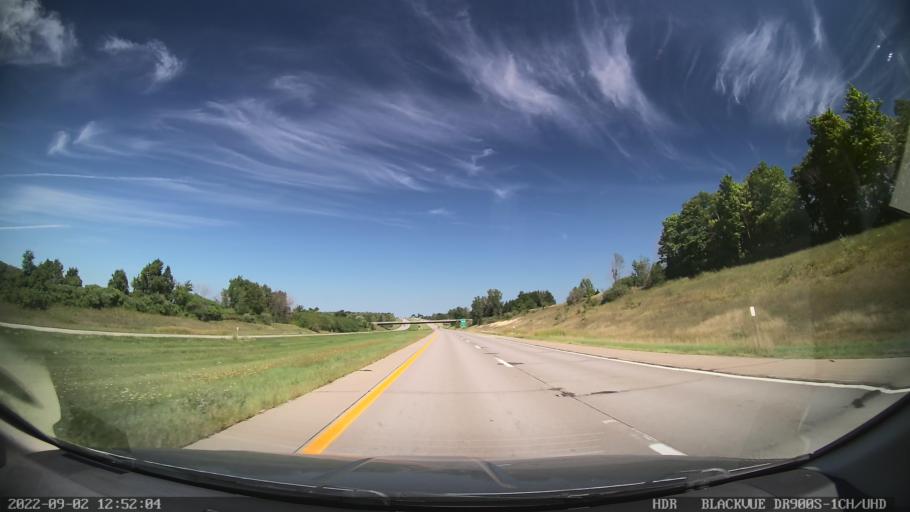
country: US
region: New York
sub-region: Livingston County
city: Avon
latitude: 42.8824
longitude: -77.6962
